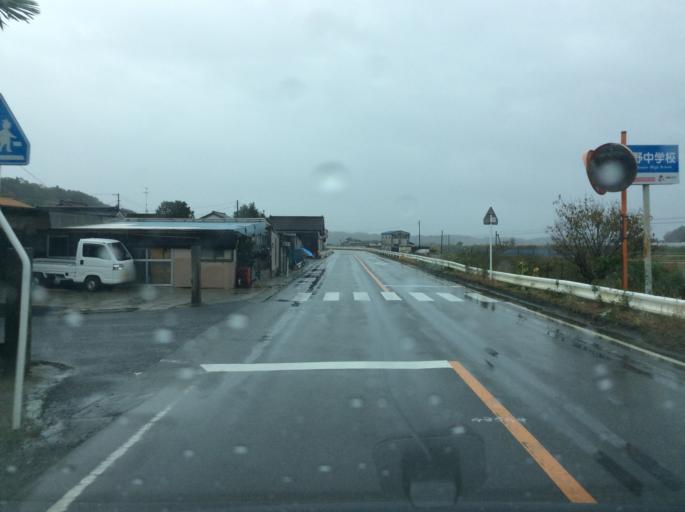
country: JP
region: Fukushima
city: Iwaki
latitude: 37.1128
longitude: 140.9365
